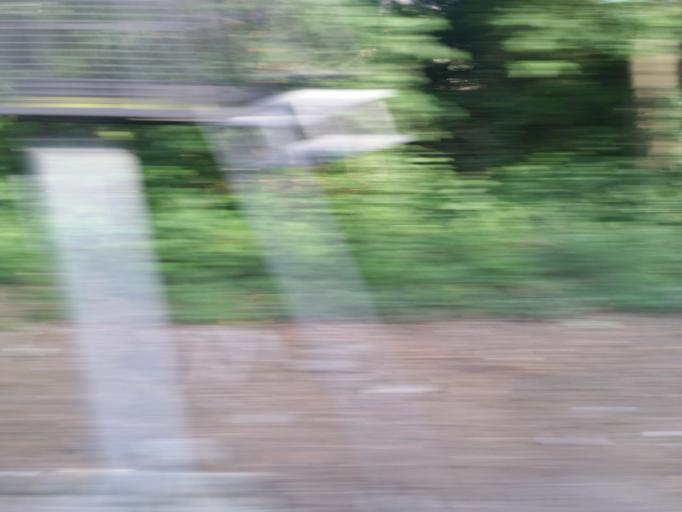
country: GB
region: England
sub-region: Greater London
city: Belsize Park
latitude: 51.5559
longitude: -0.1613
